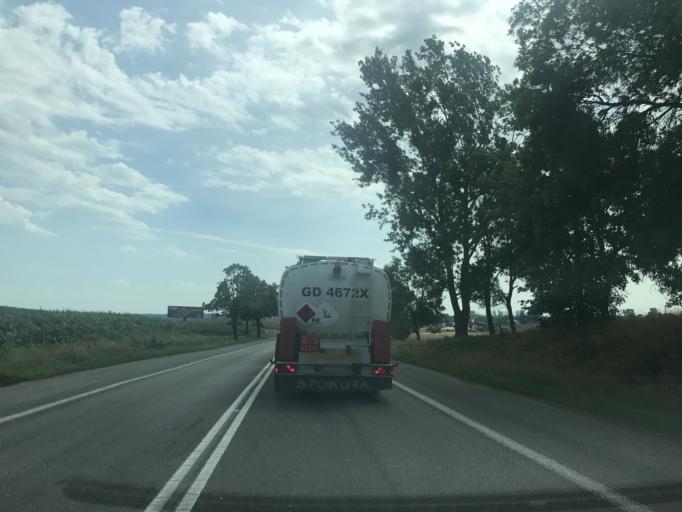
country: PL
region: Warmian-Masurian Voivodeship
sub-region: Powiat ostrodzki
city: Ostroda
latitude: 53.6559
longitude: 20.0509
